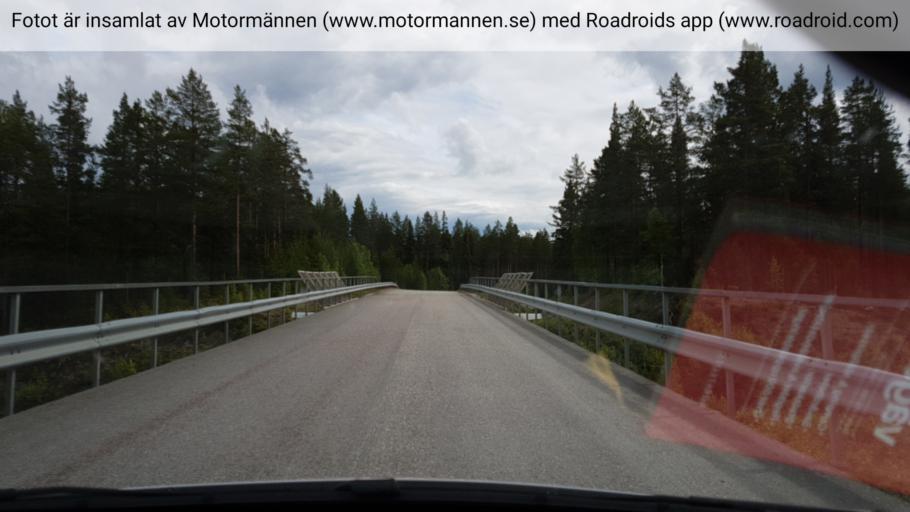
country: SE
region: Vaesternorrland
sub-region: Solleftea Kommun
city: Solleftea
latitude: 63.3861
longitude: 17.5005
